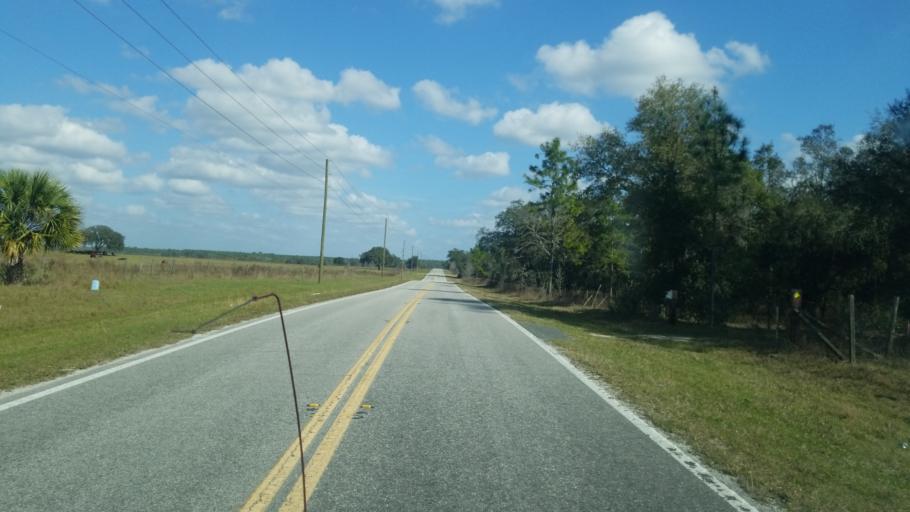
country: US
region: Florida
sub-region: Citrus County
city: Floral City
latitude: 28.7141
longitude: -82.3398
